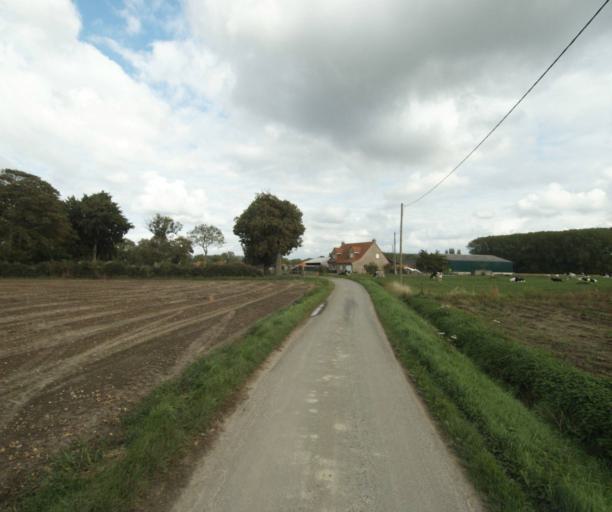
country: FR
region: Nord-Pas-de-Calais
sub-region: Departement du Nord
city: Ennetieres-en-Weppes
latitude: 50.6514
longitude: 2.9315
